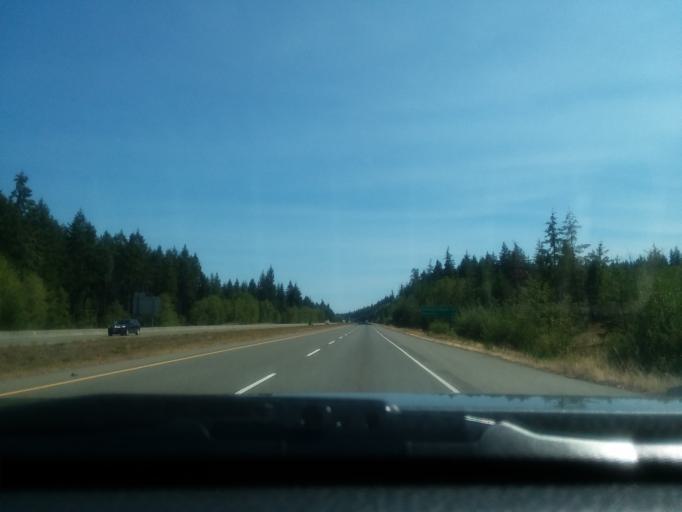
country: CA
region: British Columbia
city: Port Alberni
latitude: 49.4291
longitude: -124.7382
